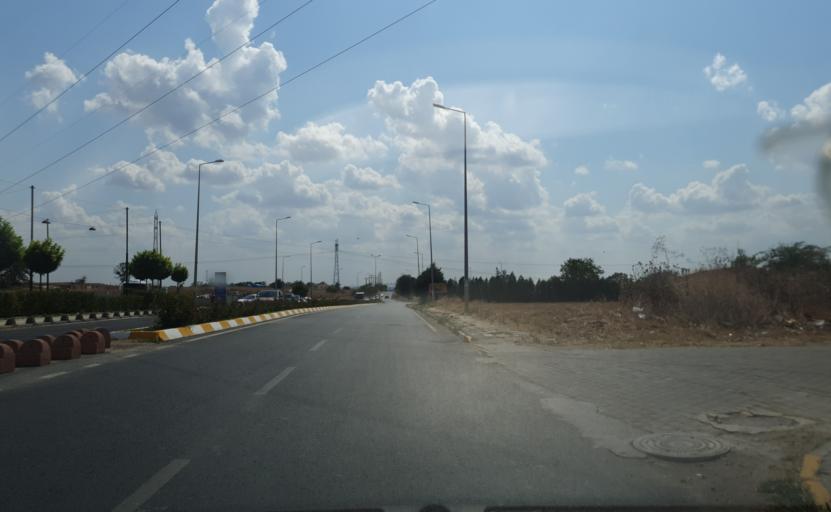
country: TR
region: Kirklareli
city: Luleburgaz
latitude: 41.3856
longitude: 27.3470
